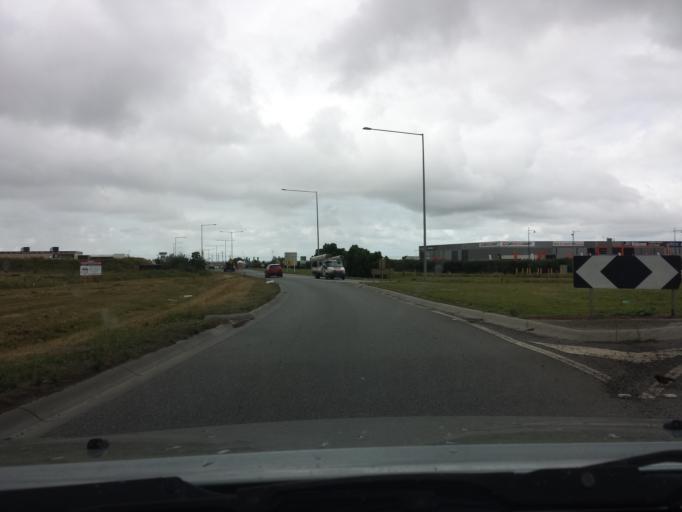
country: AU
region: Victoria
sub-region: Cardinia
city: Pakenham South
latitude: -38.0943
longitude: 145.4899
